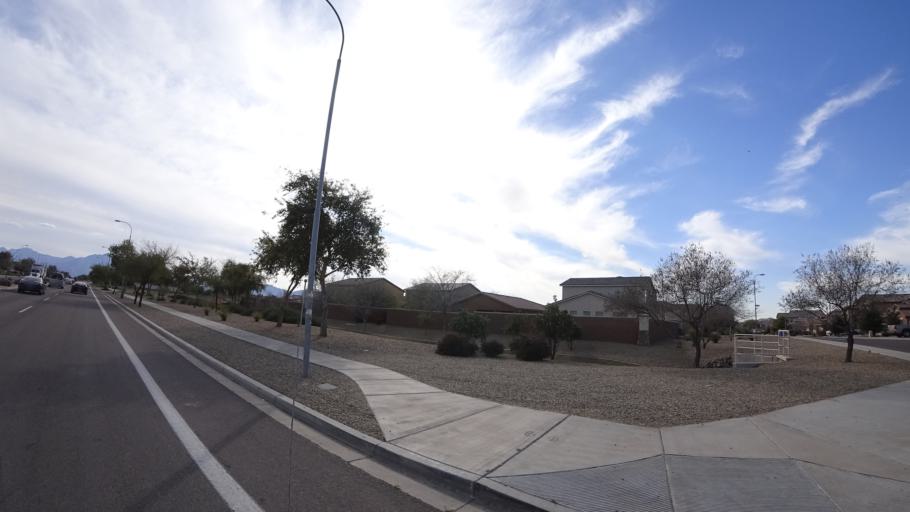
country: US
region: Arizona
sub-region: Maricopa County
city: Tolleson
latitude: 33.4263
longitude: -112.2726
